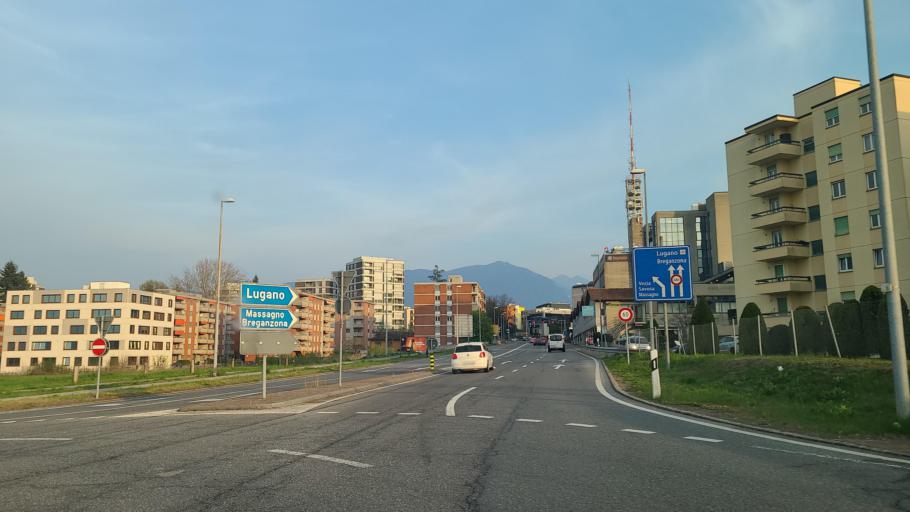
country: CH
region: Ticino
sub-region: Lugano District
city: Massagno
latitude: 46.0133
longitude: 8.9340
